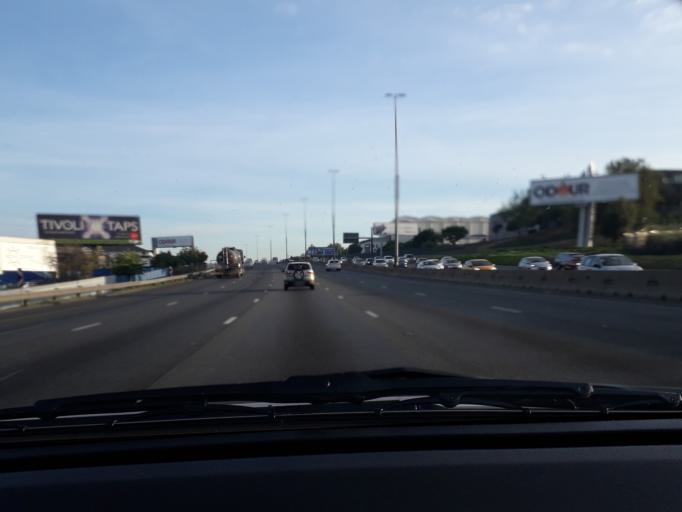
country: ZA
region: Gauteng
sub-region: City of Johannesburg Metropolitan Municipality
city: Midrand
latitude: -26.0039
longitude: 28.1207
